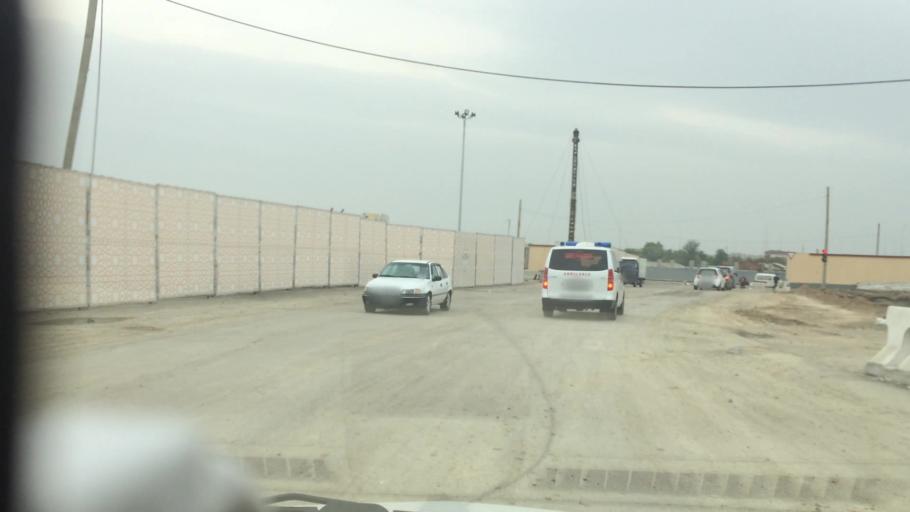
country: UZ
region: Toshkent
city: Salor
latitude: 41.3065
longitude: 69.3387
